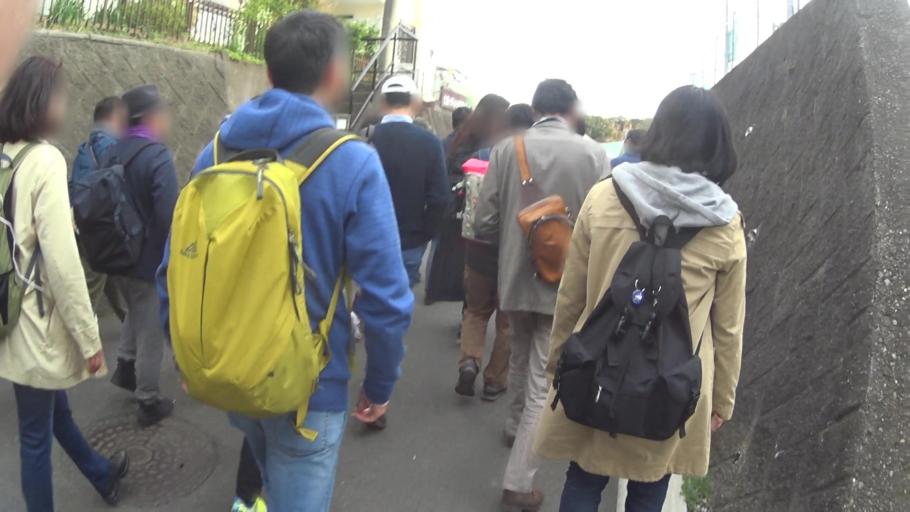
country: JP
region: Kanagawa
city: Fujisawa
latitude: 35.3141
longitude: 139.4916
